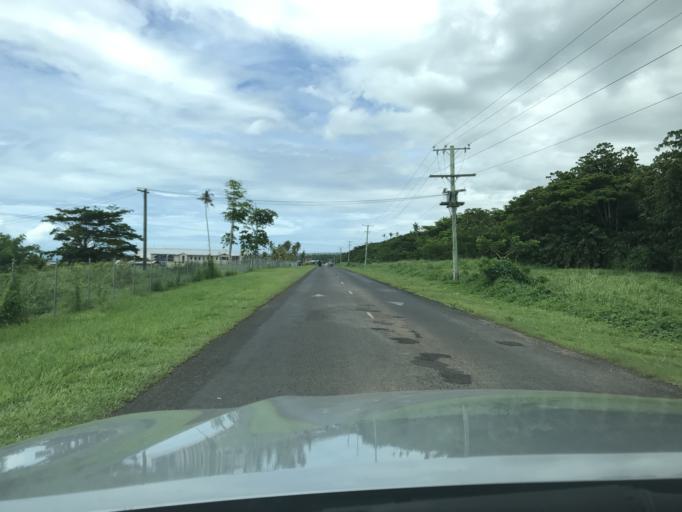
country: WS
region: A'ana
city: Satapuala
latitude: -13.8338
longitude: -172.0020
